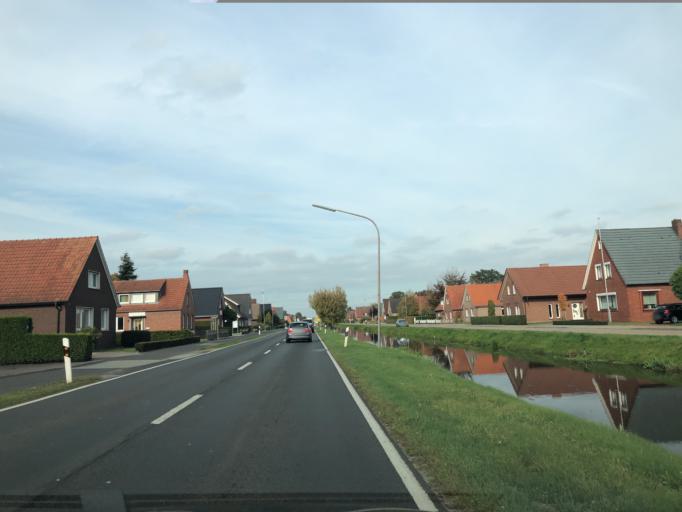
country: DE
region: Lower Saxony
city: Papenburg
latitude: 53.0589
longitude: 7.4533
